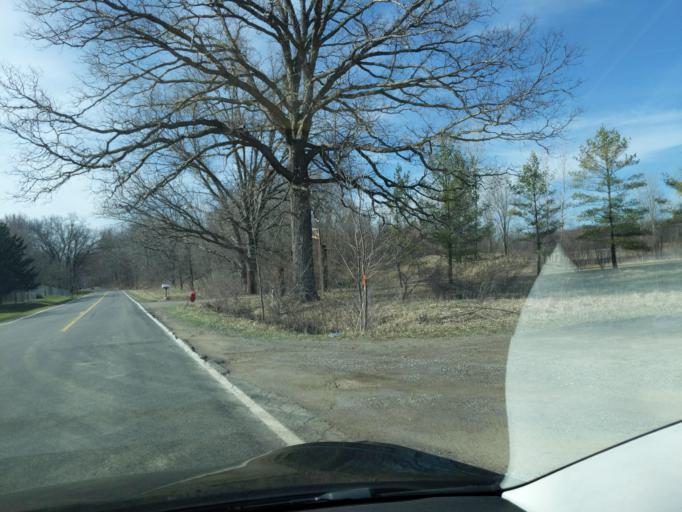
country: US
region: Michigan
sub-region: Ingham County
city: Stockbridge
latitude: 42.4830
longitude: -84.2135
